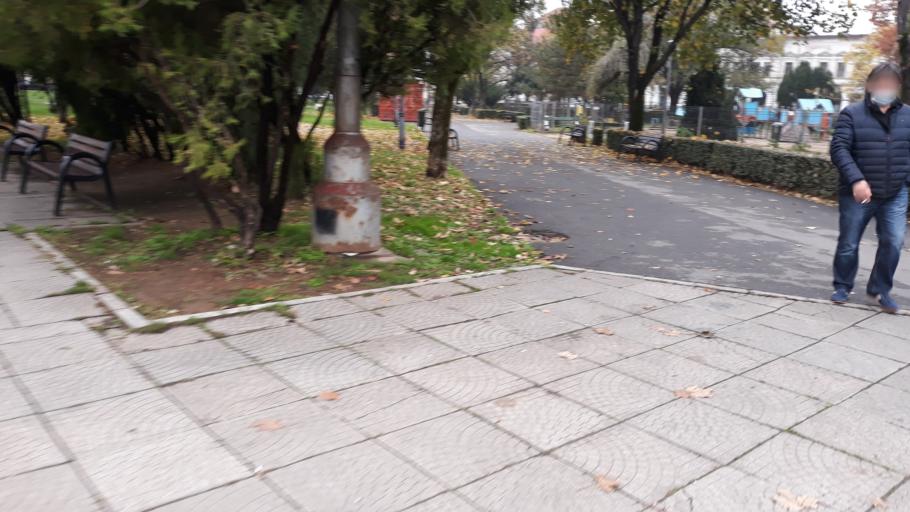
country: RO
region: Bihor
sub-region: Comuna Biharea
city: Oradea
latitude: 47.0534
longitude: 21.9342
